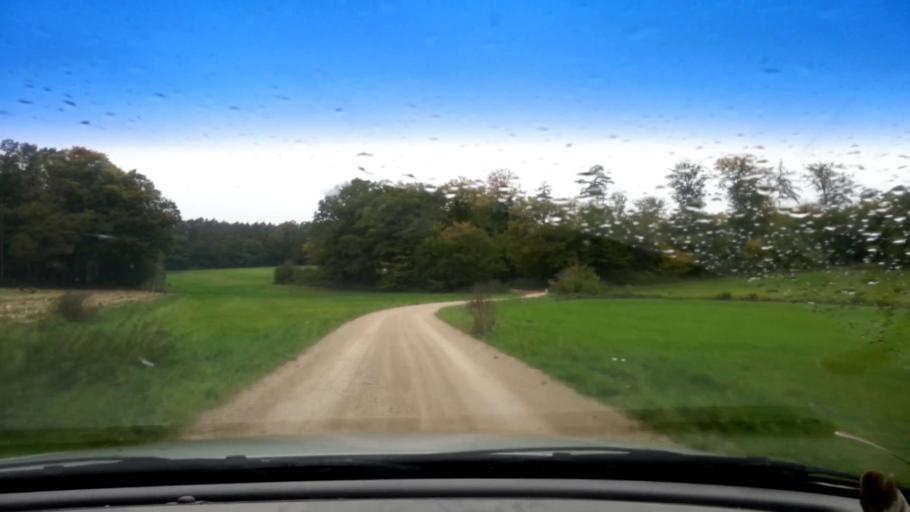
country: DE
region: Bavaria
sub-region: Upper Franconia
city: Burgwindheim
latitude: 49.8334
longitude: 10.6459
